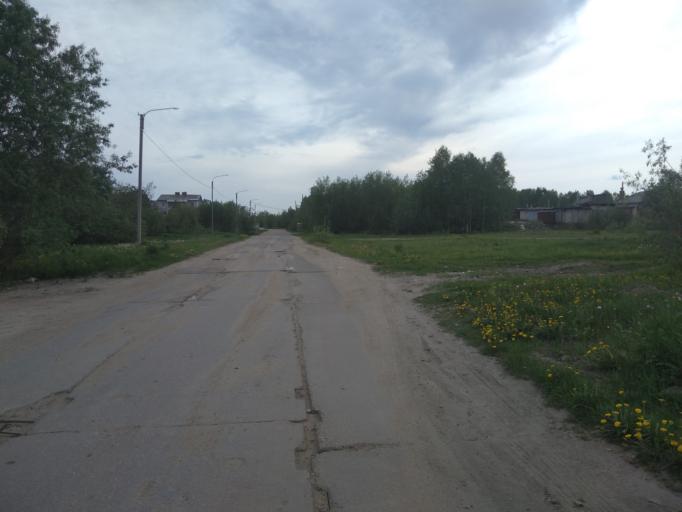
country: RU
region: Komi Republic
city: Pechora
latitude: 65.1427
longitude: 57.2472
